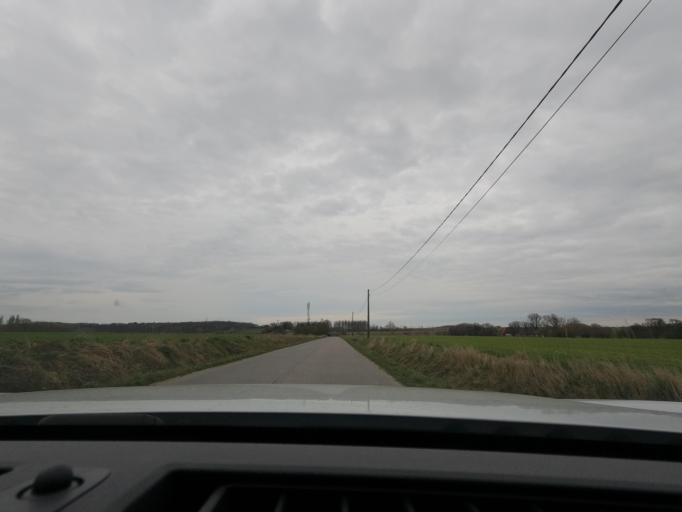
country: BE
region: Wallonia
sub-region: Province du Hainaut
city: Brugelette
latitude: 50.6294
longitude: 3.8612
